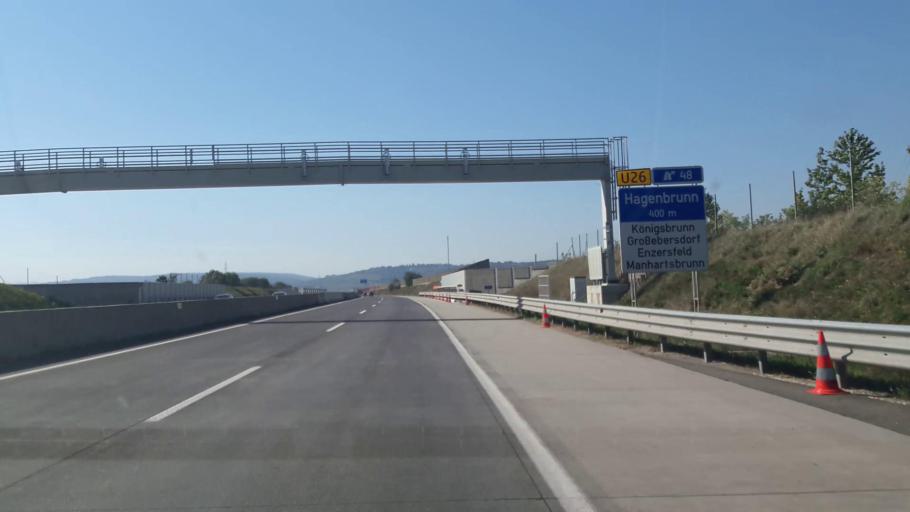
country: AT
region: Lower Austria
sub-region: Politischer Bezirk Mistelbach
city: Grossebersdorf
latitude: 48.3480
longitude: 16.4496
